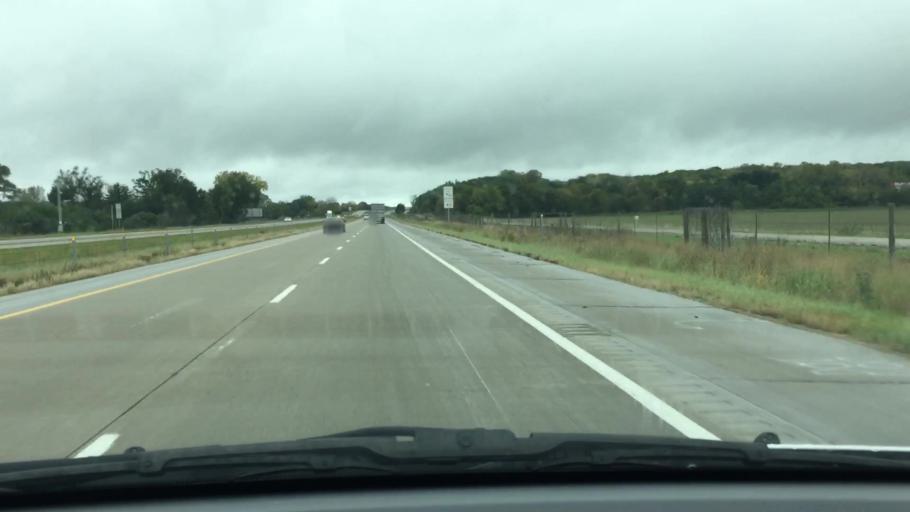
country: US
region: Iowa
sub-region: Jasper County
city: Colfax
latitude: 41.6898
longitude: -93.2584
